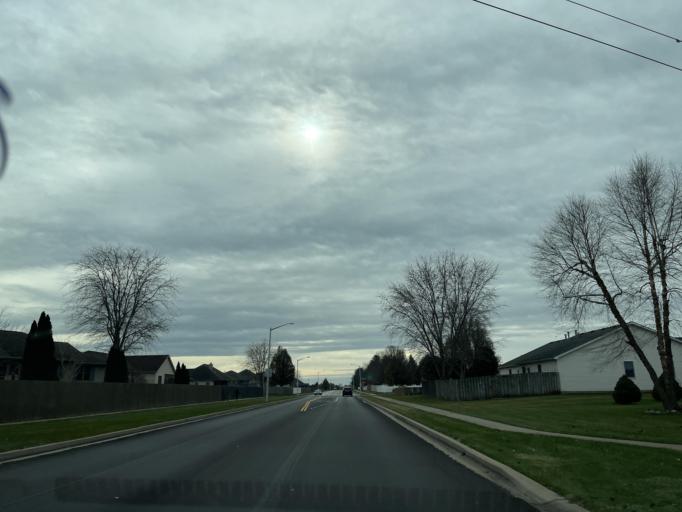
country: US
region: Illinois
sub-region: Sangamon County
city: Jerome
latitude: 39.7783
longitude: -89.7299
